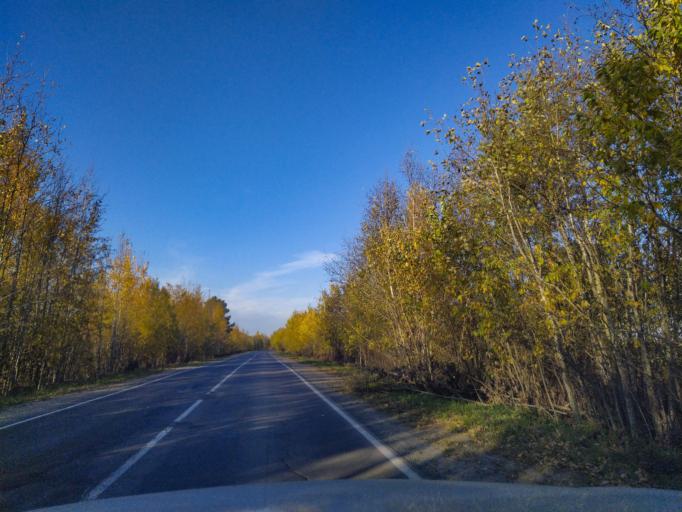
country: RU
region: Leningrad
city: Siverskiy
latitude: 59.3147
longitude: 30.0334
